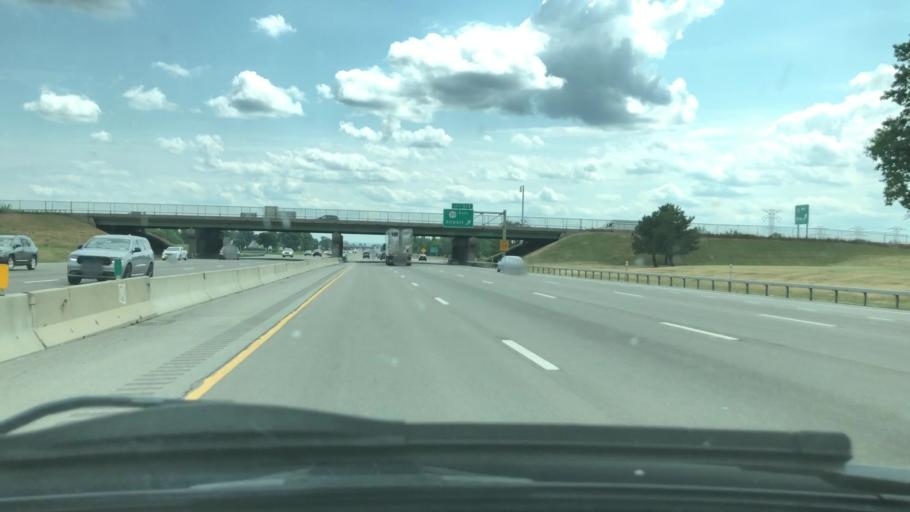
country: US
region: New York
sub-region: Erie County
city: Cheektowaga
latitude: 42.9335
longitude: -78.7668
